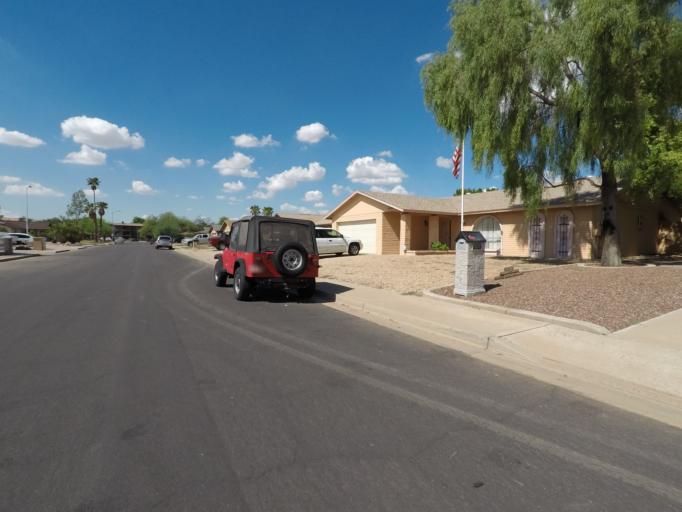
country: US
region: Arizona
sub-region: Maricopa County
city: Tempe
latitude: 33.4283
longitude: -111.8779
